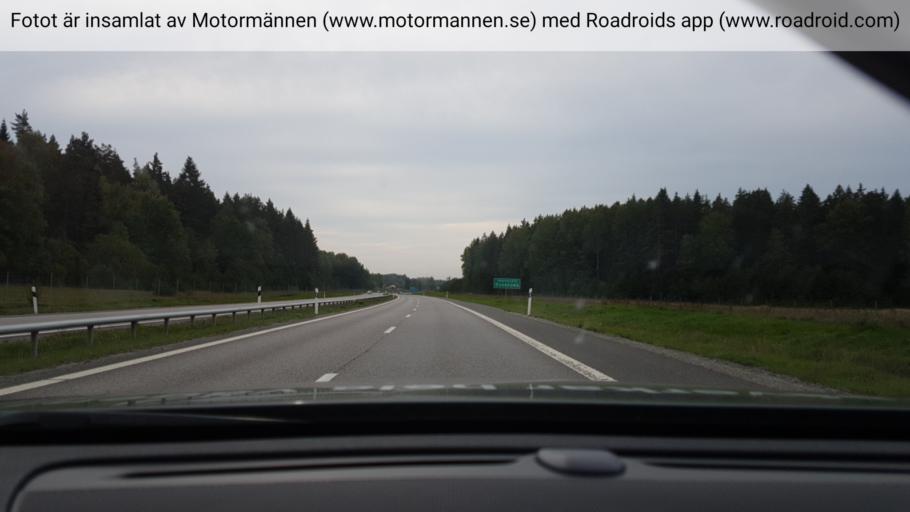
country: SE
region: Stockholm
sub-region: Nynashamns Kommun
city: Osmo
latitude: 59.0083
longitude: 17.9422
